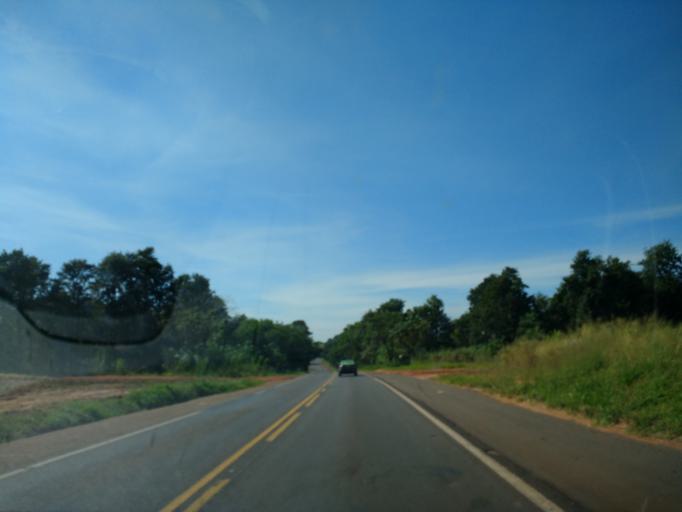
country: BR
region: Parana
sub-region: Alto Piquiri
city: Alto Piquiri
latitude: -23.8928
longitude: -53.4509
